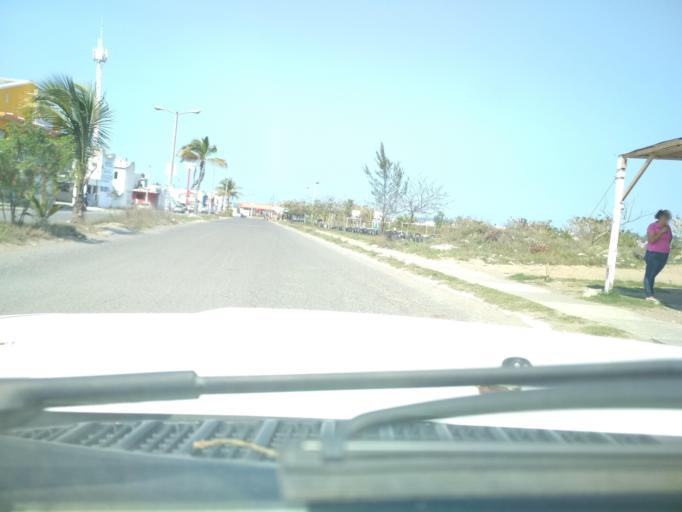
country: MX
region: Veracruz
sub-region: Veracruz
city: Los Torrentes
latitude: 19.1998
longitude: -96.2079
